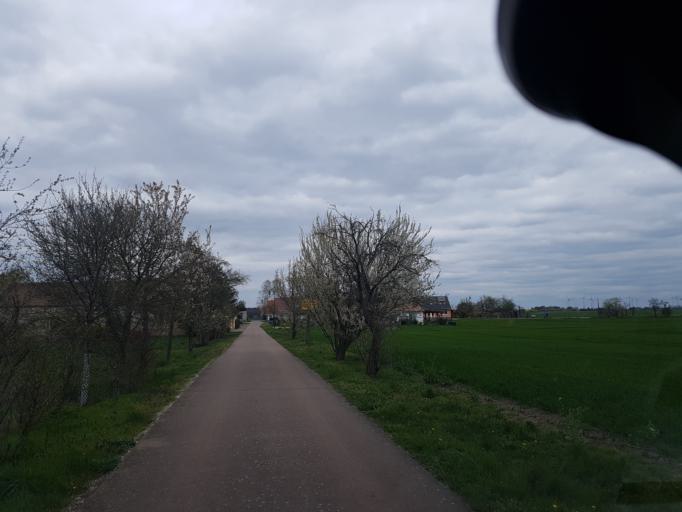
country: DE
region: Brandenburg
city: Juterbog
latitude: 51.9144
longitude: 13.0976
